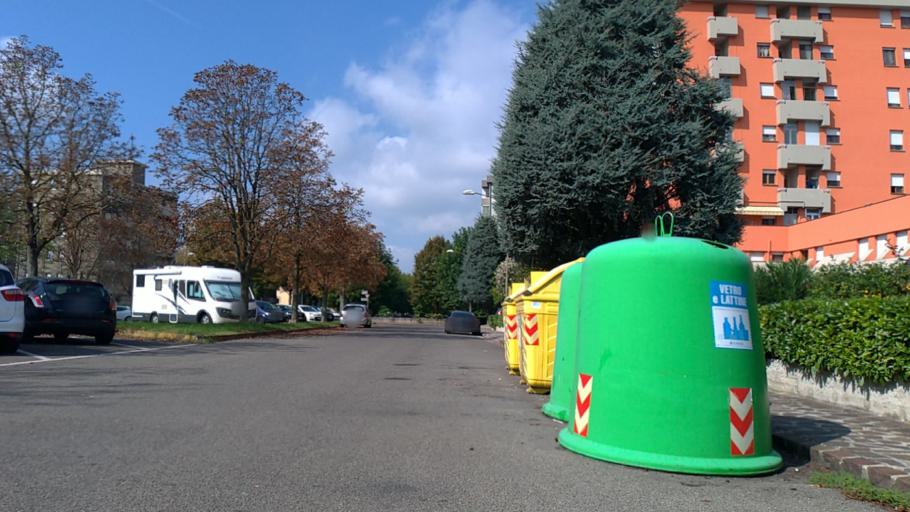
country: IT
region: Emilia-Romagna
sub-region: Provincia di Modena
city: Carpi Centro
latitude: 44.7718
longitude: 10.8729
